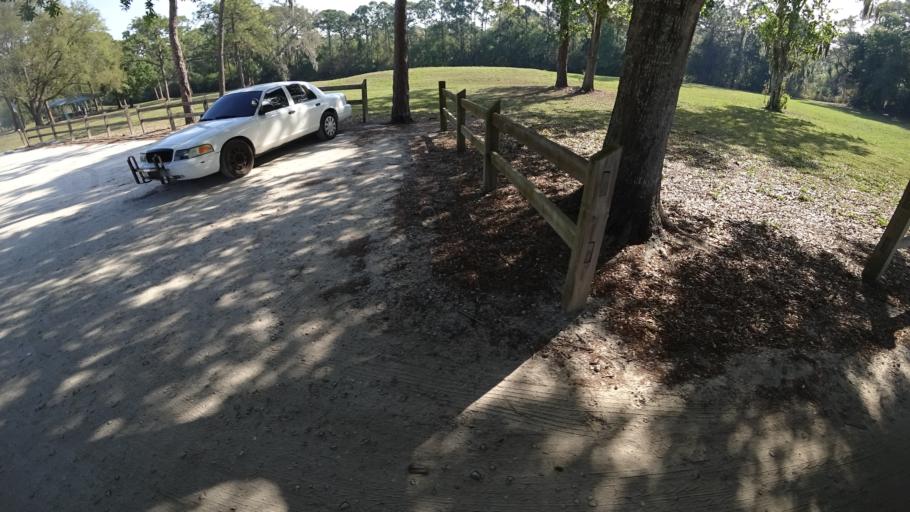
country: US
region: Florida
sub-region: Manatee County
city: Whitfield
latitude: 27.4115
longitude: -82.5516
